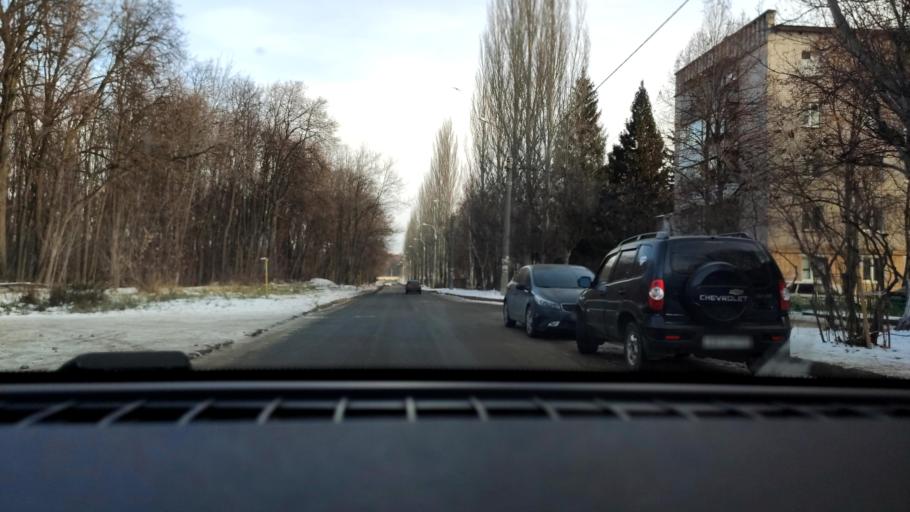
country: RU
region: Samara
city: Petra-Dubrava
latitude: 53.3053
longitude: 50.2729
